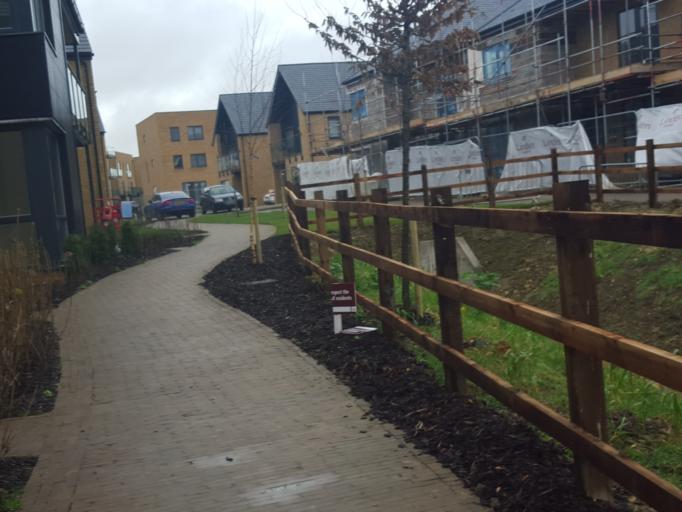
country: GB
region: England
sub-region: Essex
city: Harlow
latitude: 51.7705
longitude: 0.1421
